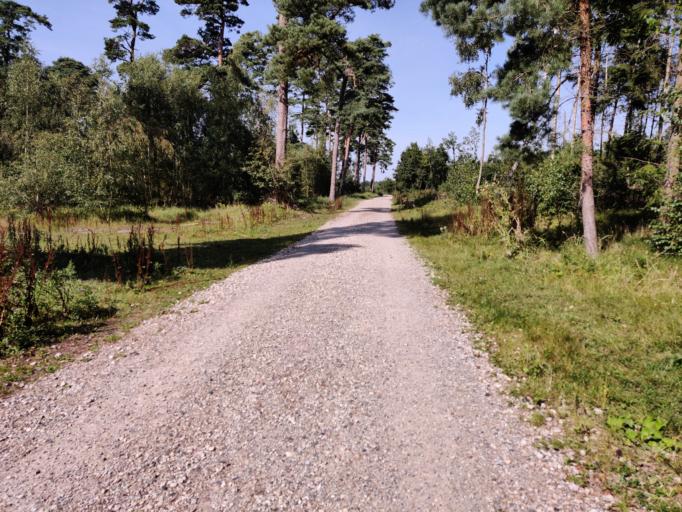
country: DK
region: Zealand
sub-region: Guldborgsund Kommune
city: Nykobing Falster
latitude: 54.6373
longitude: 11.9572
